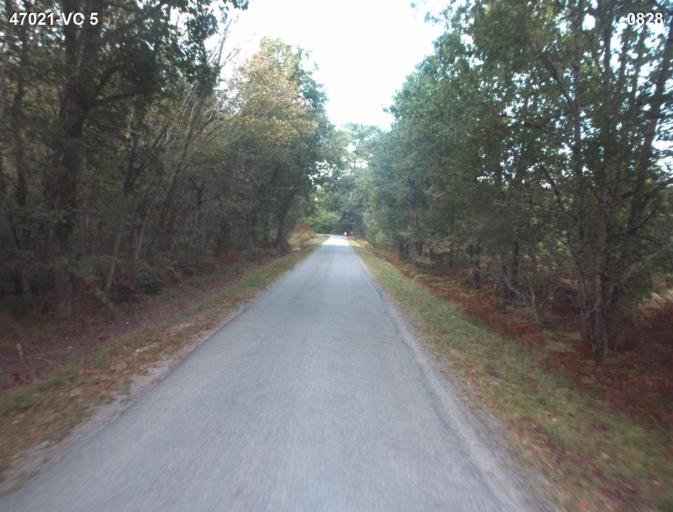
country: FR
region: Aquitaine
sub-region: Departement du Lot-et-Garonne
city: Barbaste
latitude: 44.1430
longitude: 0.2862
